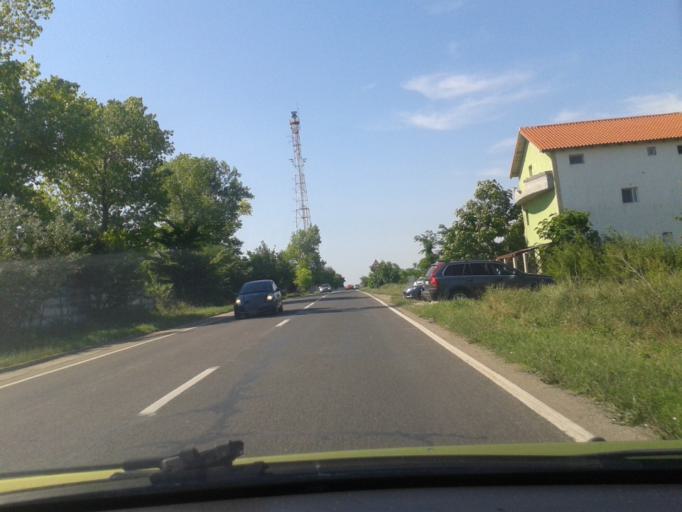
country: RO
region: Constanta
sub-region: Municipiul Mangalia
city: Mangalia
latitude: 43.7793
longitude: 28.5781
